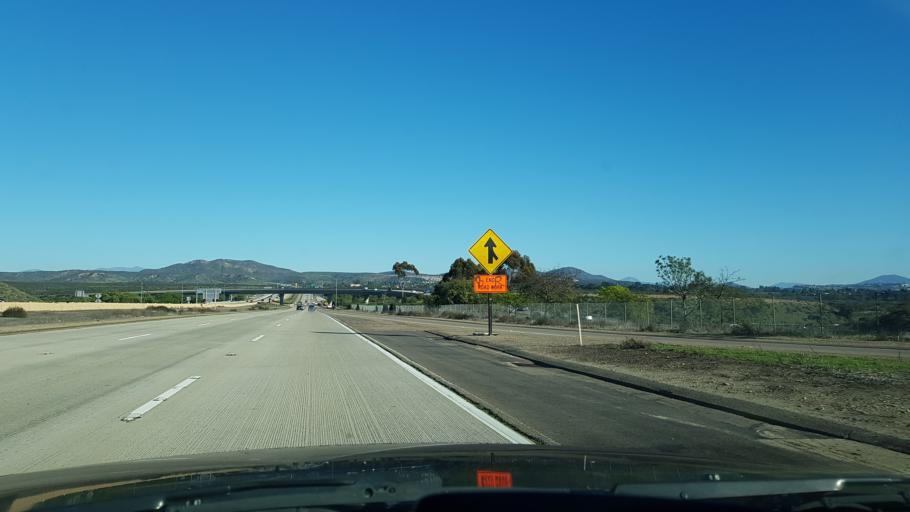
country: US
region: California
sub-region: San Diego County
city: La Mesa
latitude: 32.8416
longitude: -117.1260
